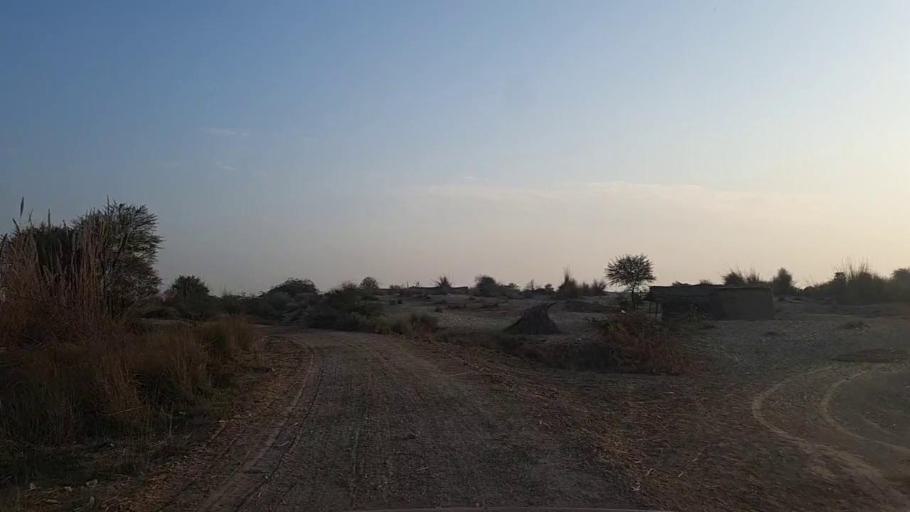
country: PK
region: Sindh
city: Daur
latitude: 26.4835
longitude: 68.4283
